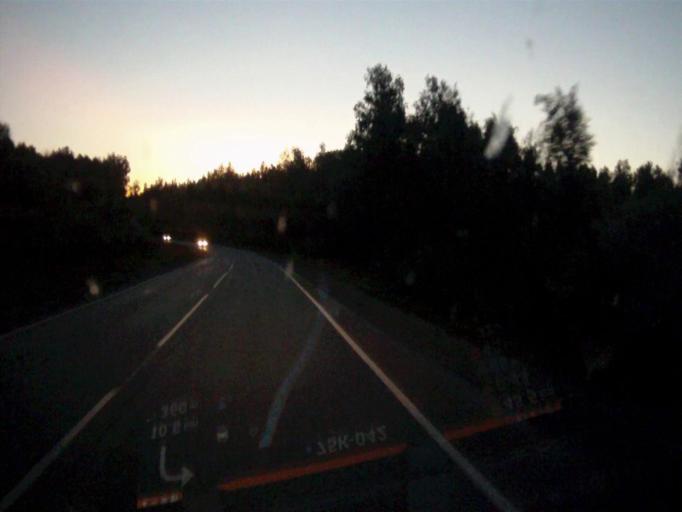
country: RU
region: Chelyabinsk
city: Timiryazevskiy
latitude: 55.2059
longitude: 60.7592
